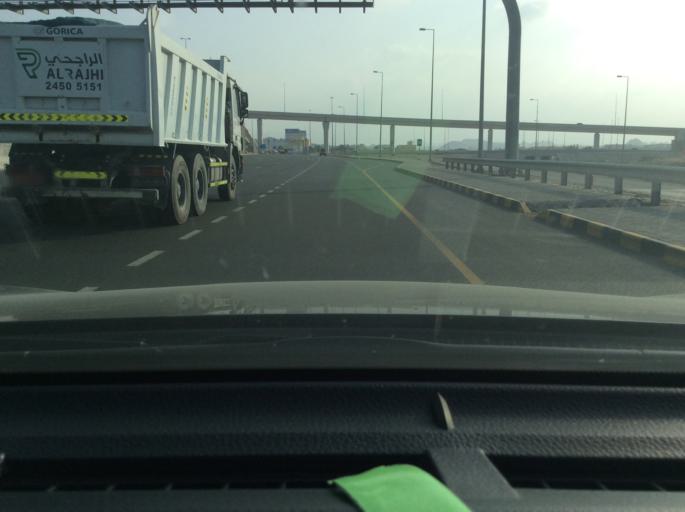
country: OM
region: Muhafazat Masqat
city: Bawshar
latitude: 23.5055
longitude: 58.5001
